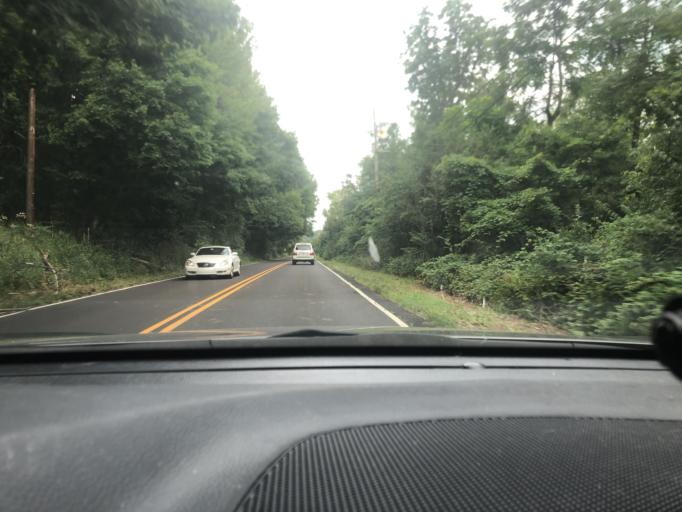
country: US
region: Pennsylvania
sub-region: Montgomery County
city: Spring House
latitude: 40.1895
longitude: -75.2345
